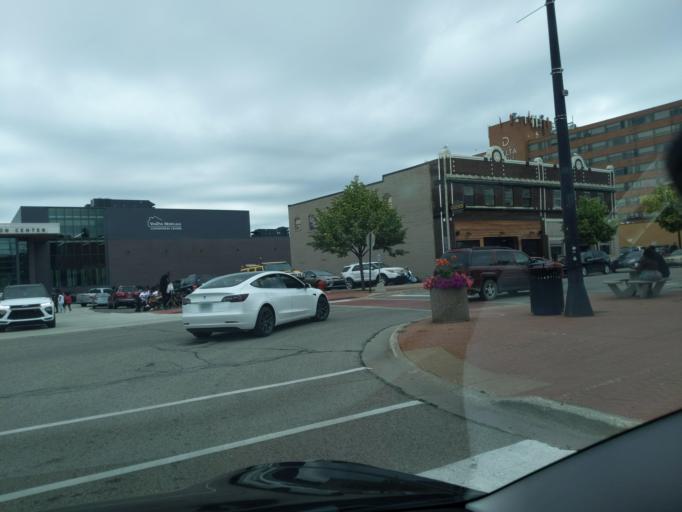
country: US
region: Michigan
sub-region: Muskegon County
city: Muskegon
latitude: 43.2344
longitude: -86.2544
